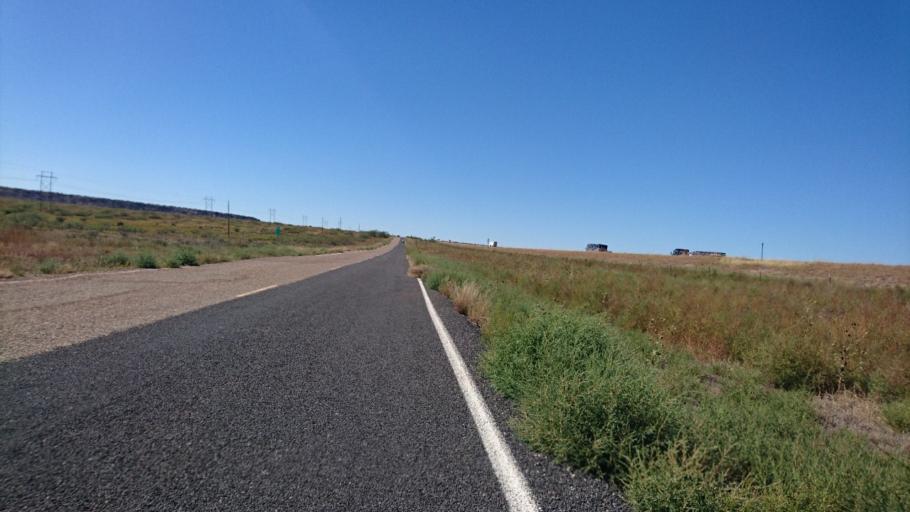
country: US
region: New Mexico
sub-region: Quay County
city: Tucumcari
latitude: 35.0830
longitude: -104.1109
